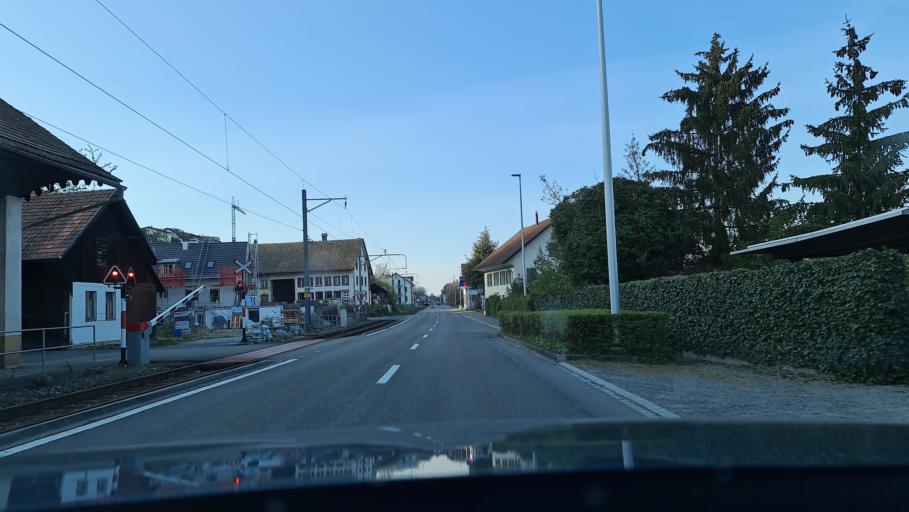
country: CH
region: Aargau
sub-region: Bezirk Kulm
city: Reinach
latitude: 47.2847
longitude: 8.1996
